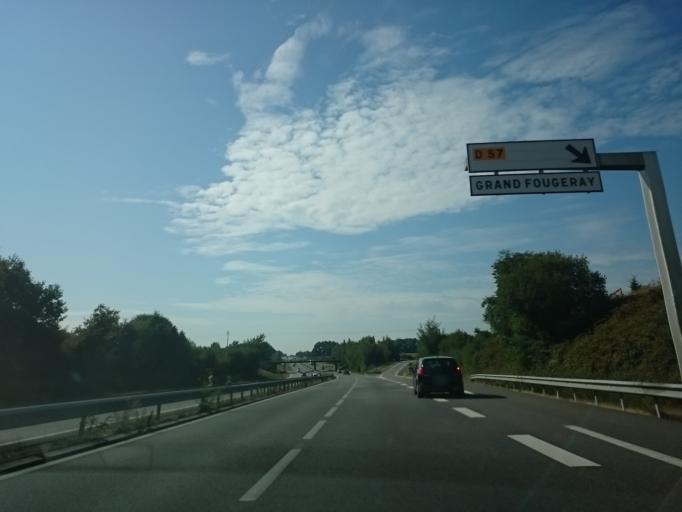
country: FR
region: Brittany
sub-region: Departement d'Ille-et-Vilaine
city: Grand-Fougeray
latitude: 47.7487
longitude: -1.7154
